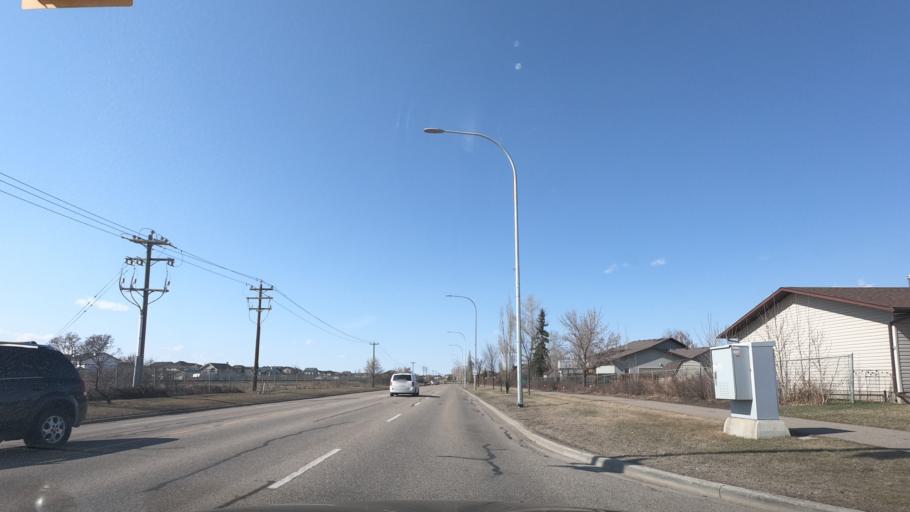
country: CA
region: Alberta
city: Airdrie
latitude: 51.2737
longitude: -114.0126
